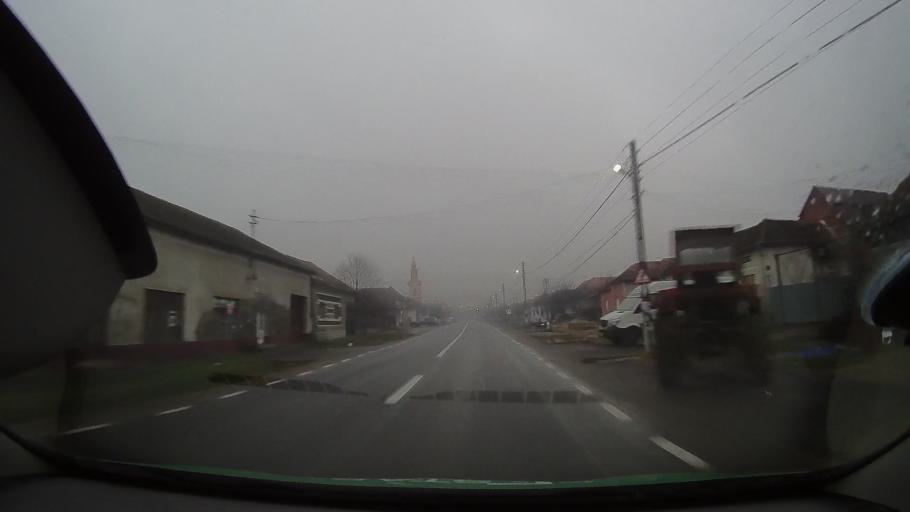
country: RO
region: Bihor
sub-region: Comuna Olcea
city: Calacea
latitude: 46.6388
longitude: 21.9559
